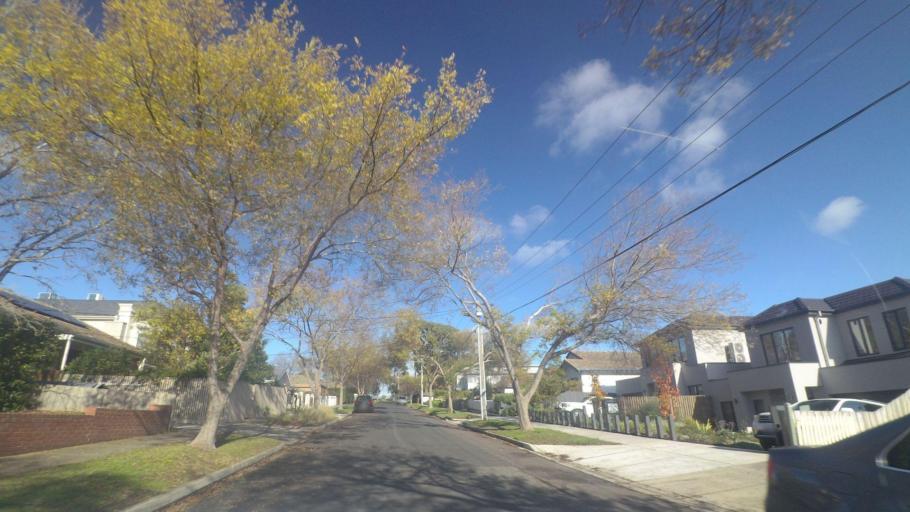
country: AU
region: Victoria
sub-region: Whitehorse
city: Mont Albert North
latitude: -37.8076
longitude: 145.1102
